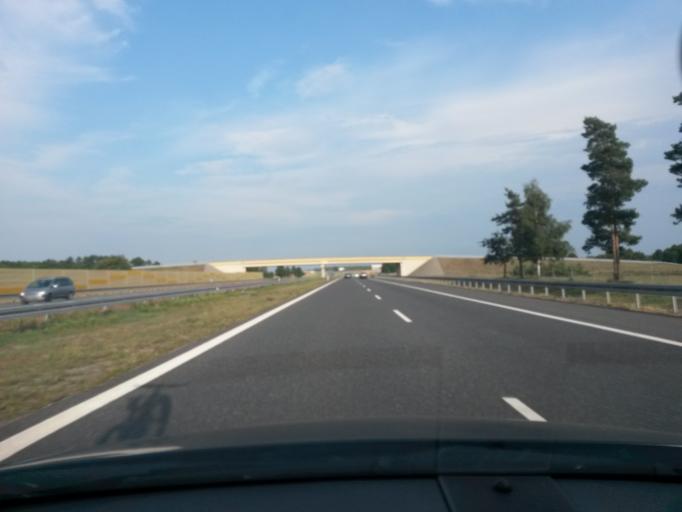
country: PL
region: Lodz Voivodeship
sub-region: Powiat zgierski
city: Ozorkow
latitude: 51.9331
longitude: 19.2762
